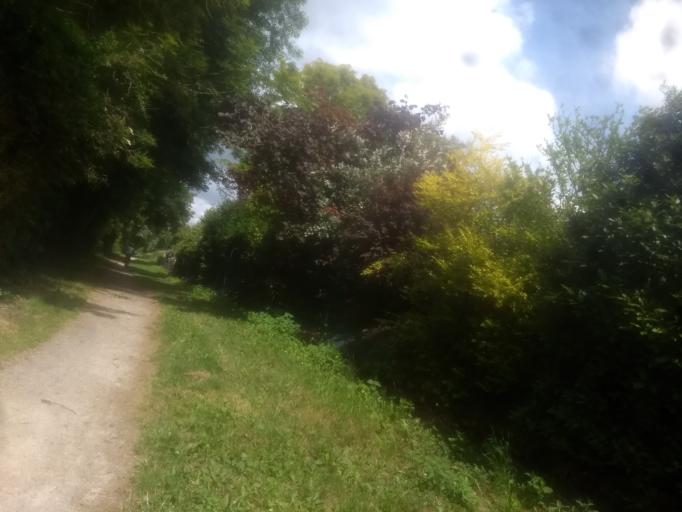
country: FR
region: Nord-Pas-de-Calais
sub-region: Departement du Pas-de-Calais
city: Sainte-Catherine
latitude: 50.3026
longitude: 2.7557
